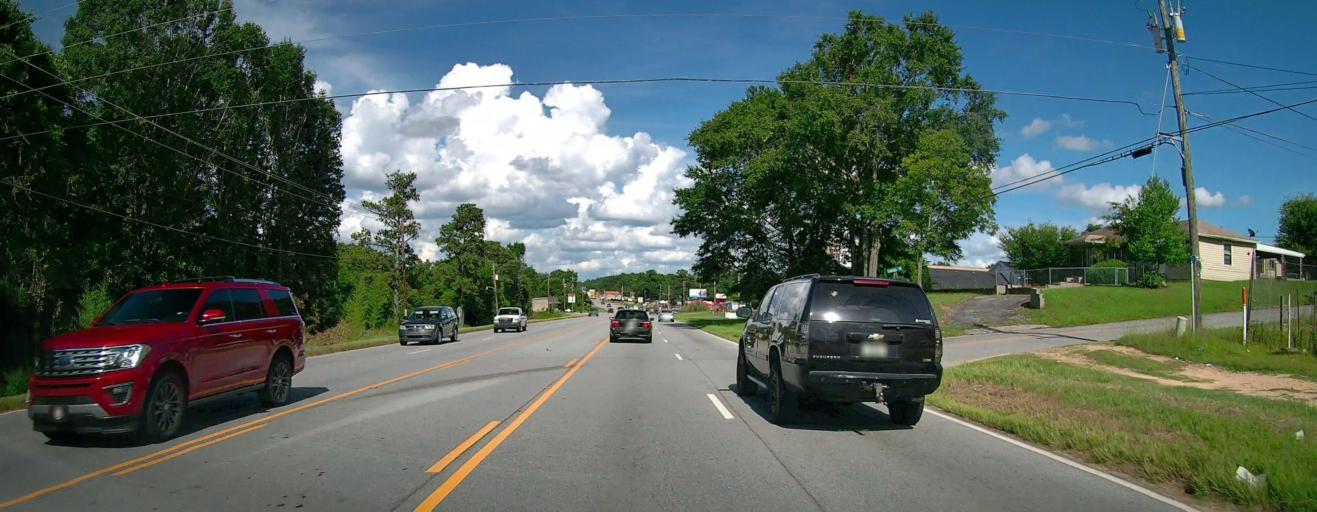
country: US
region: Alabama
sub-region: Russell County
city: Ladonia
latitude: 32.4679
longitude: -85.0746
